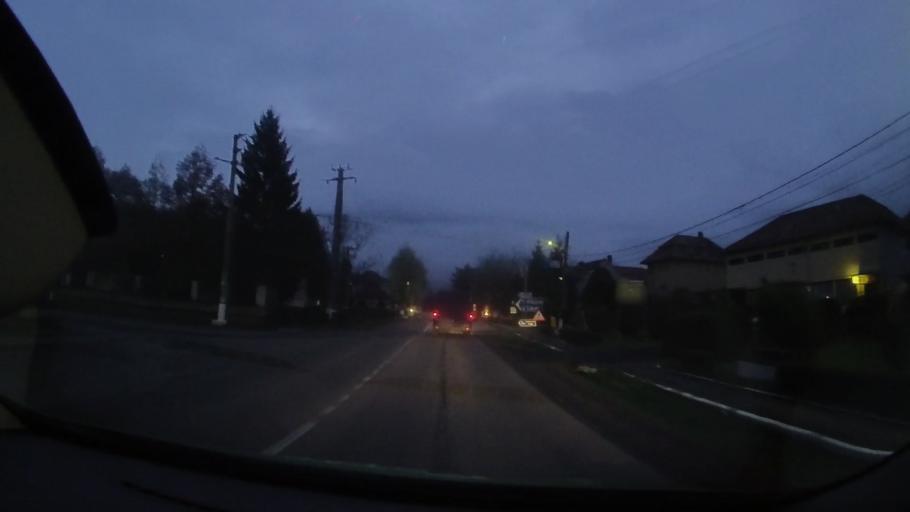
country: RO
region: Mures
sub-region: Comuna Gurghiu
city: Gurghiu
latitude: 46.7724
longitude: 24.8580
